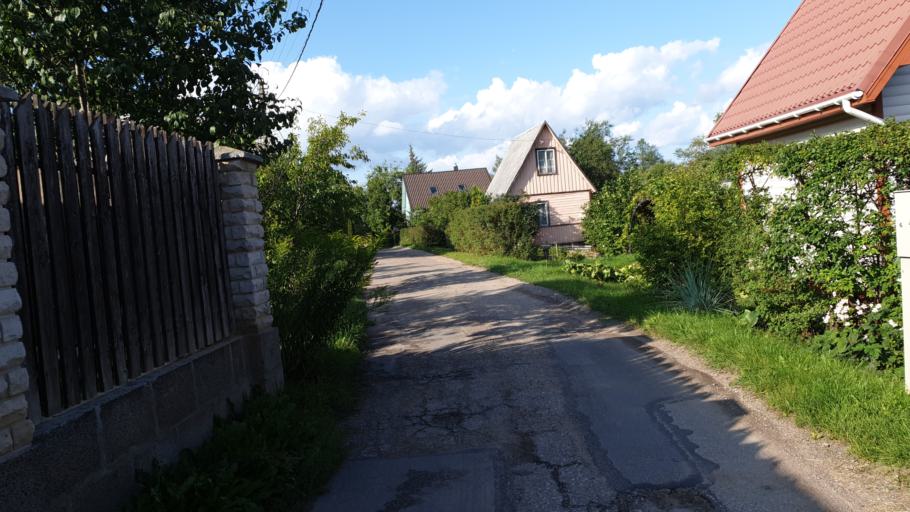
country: LT
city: Grigiskes
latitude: 54.7680
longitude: 25.0179
